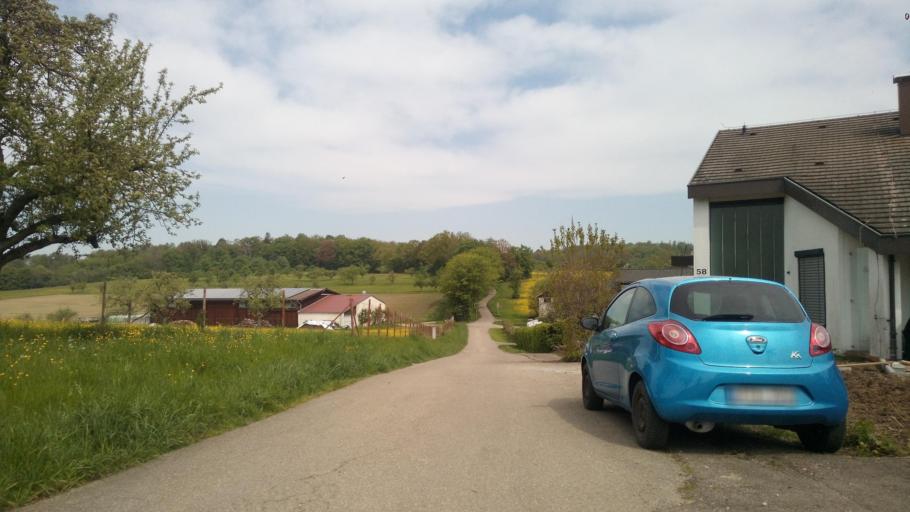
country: DE
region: Baden-Wuerttemberg
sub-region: Regierungsbezirk Stuttgart
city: Eislingen
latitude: 48.7084
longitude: 9.7038
